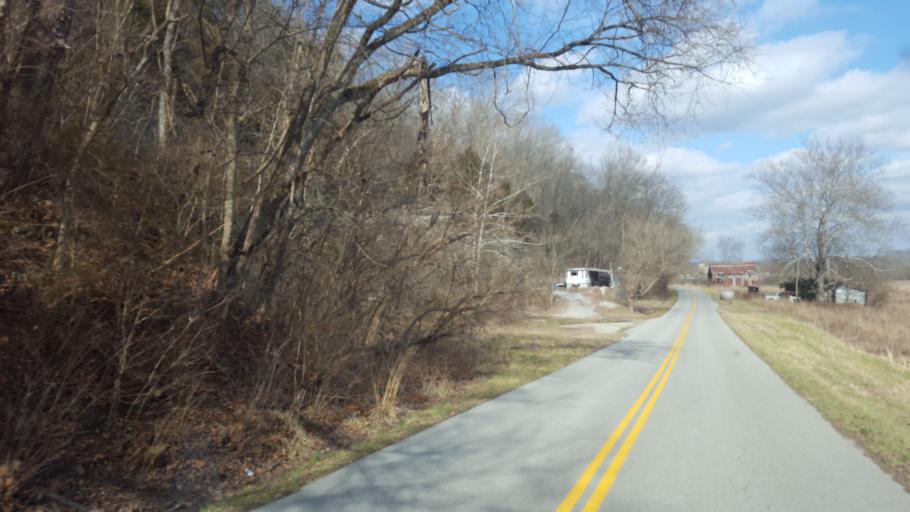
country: US
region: Kentucky
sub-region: Owen County
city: Owenton
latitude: 38.4420
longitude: -84.9619
